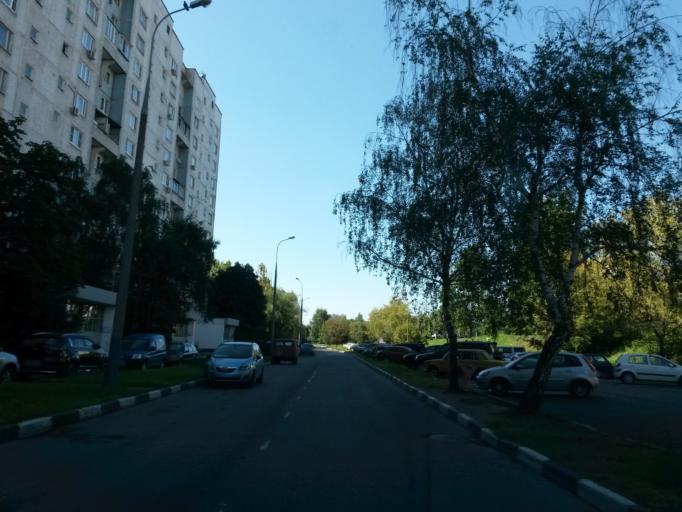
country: RU
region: Moscow
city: Mar'ino
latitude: 55.6490
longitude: 37.7159
